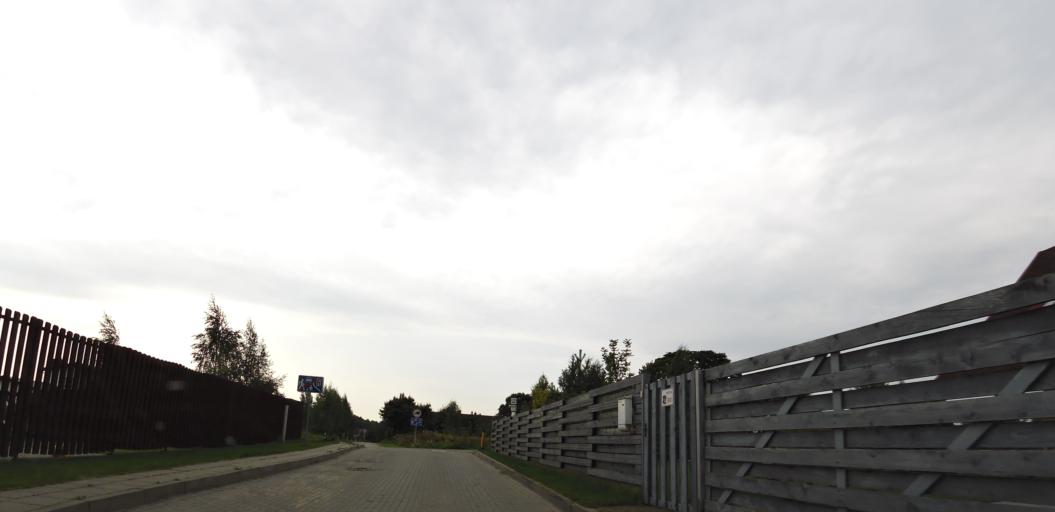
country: LT
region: Vilnius County
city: Pasilaiciai
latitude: 54.7580
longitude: 25.2297
